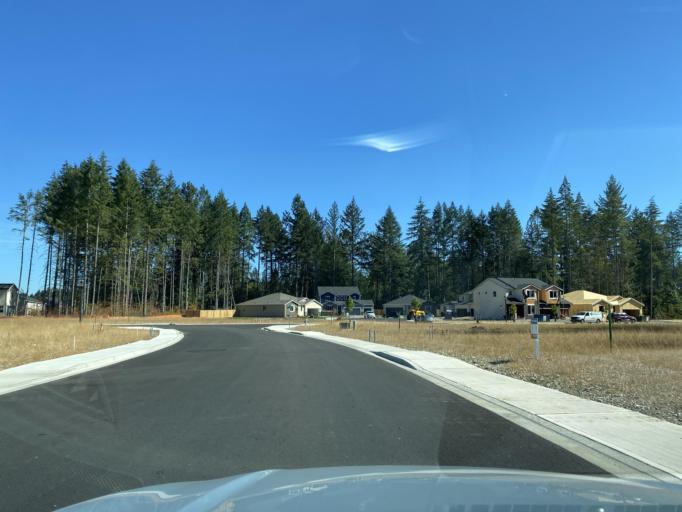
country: US
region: Washington
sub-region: Pierce County
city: McMillin
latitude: 47.0936
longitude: -122.2550
